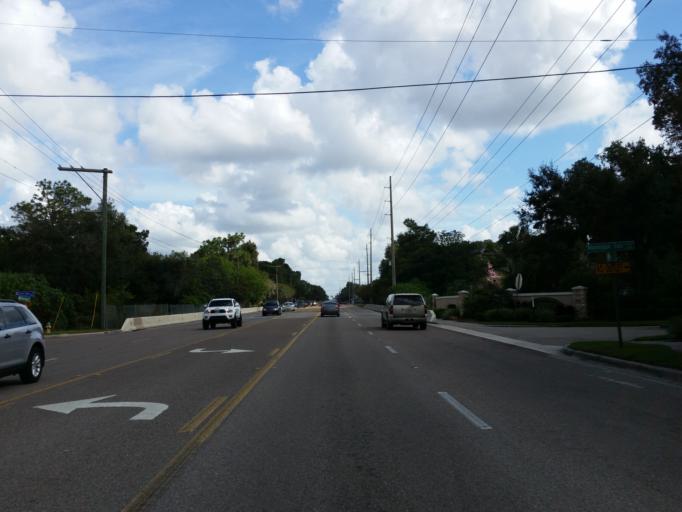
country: US
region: Florida
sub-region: Hillsborough County
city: Riverview
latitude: 27.8936
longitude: -82.2994
